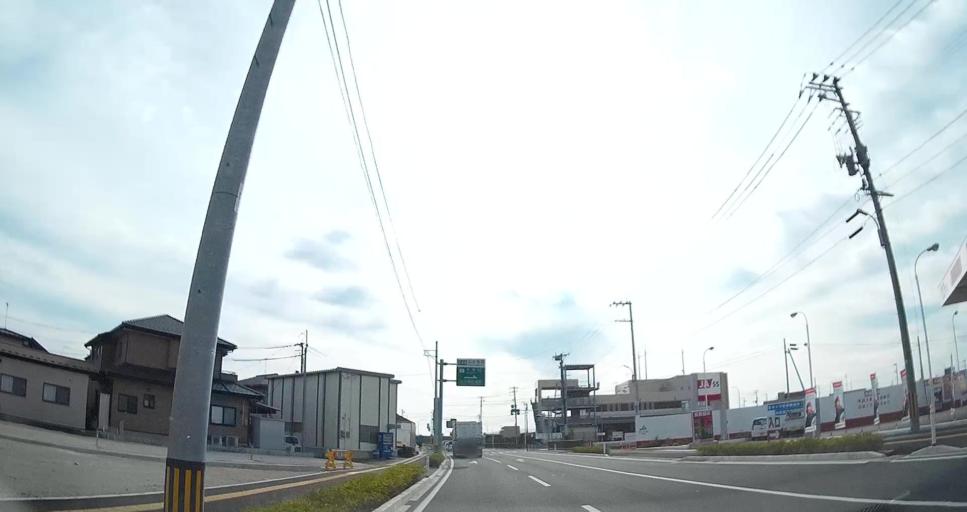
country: JP
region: Miyagi
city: Sendai
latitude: 38.2123
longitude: 140.9340
